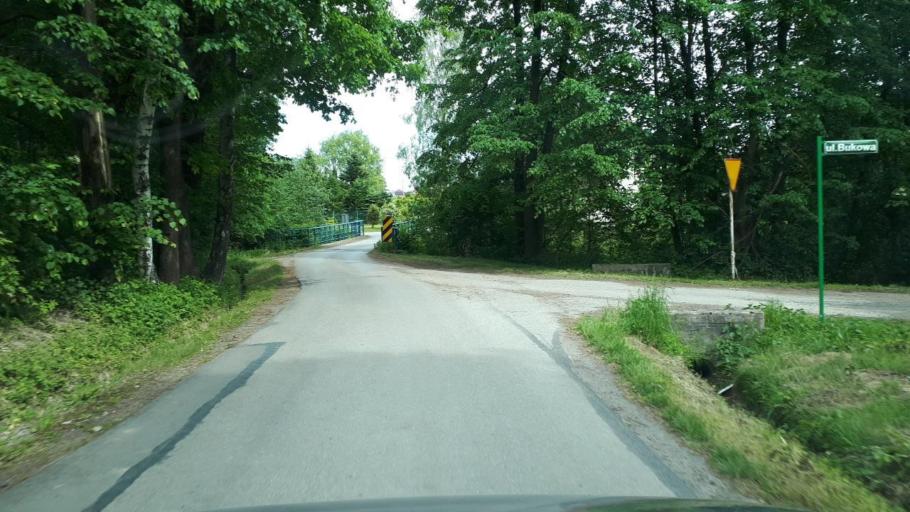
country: PL
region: Silesian Voivodeship
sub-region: Powiat bielski
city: Pisarzowice
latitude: 49.8850
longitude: 19.1310
